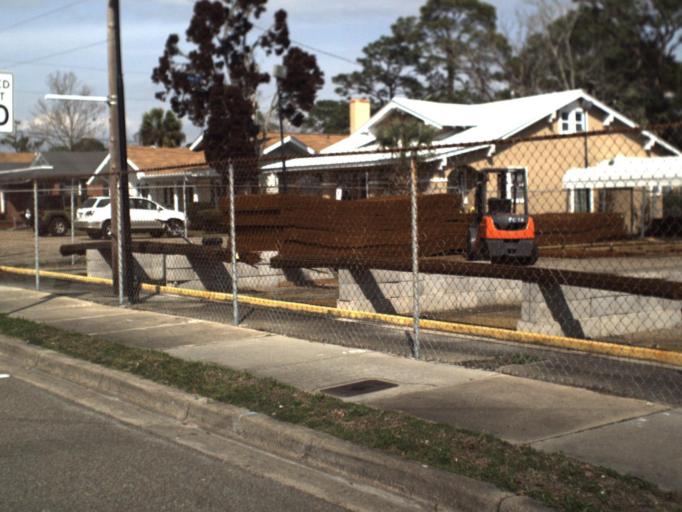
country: US
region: Florida
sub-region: Bay County
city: Panama City
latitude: 30.1662
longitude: -85.6602
